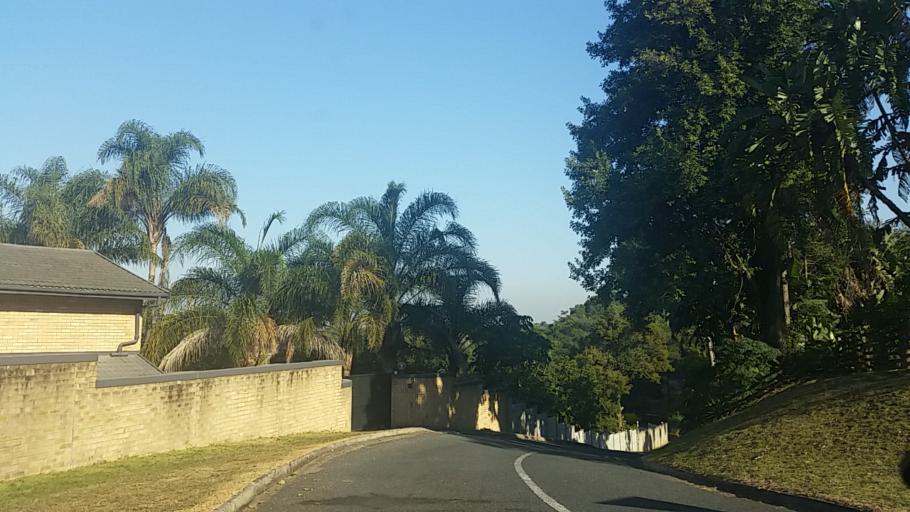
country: ZA
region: KwaZulu-Natal
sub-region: eThekwini Metropolitan Municipality
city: Berea
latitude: -29.8491
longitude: 30.9117
